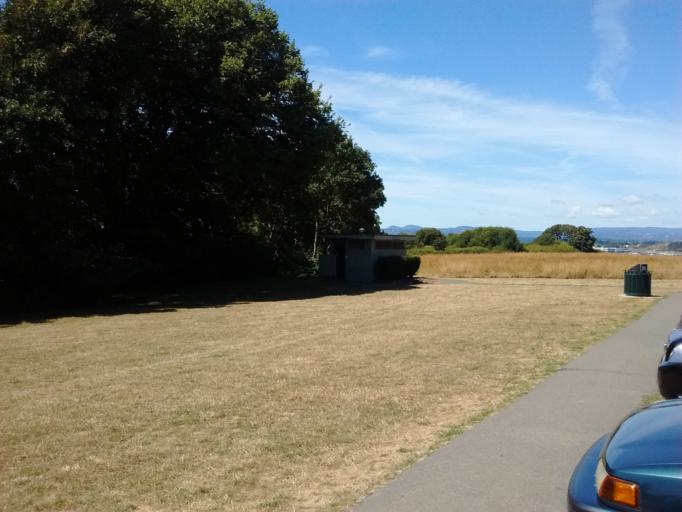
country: CA
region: British Columbia
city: Victoria
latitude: 48.4104
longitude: -123.3745
